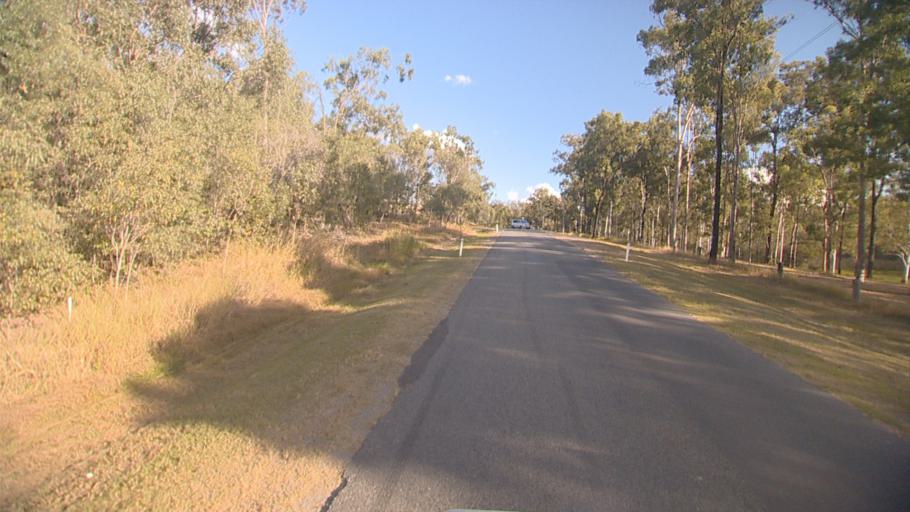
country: AU
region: Queensland
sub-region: Logan
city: North Maclean
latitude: -27.7445
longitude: 152.9414
